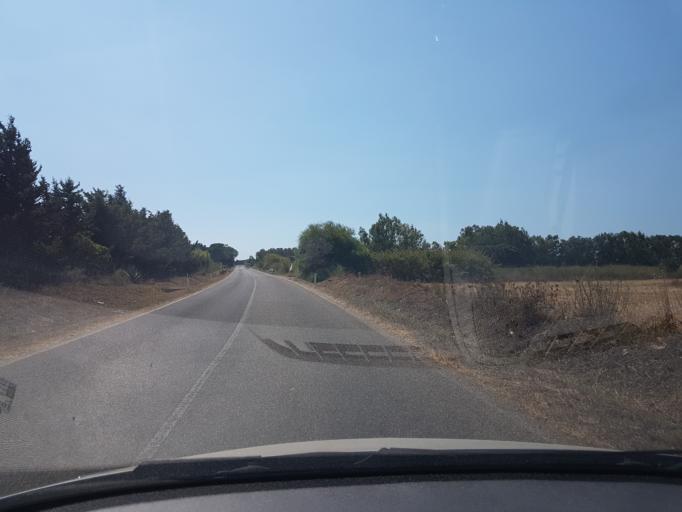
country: IT
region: Sardinia
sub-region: Provincia di Oristano
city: Riola Sardo
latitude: 39.9971
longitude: 8.4817
